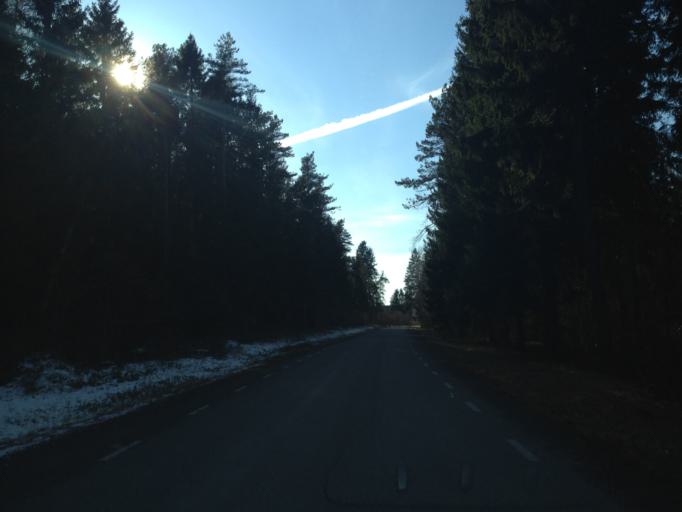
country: EE
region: Harju
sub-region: Nissi vald
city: Turba
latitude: 59.1382
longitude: 24.1738
